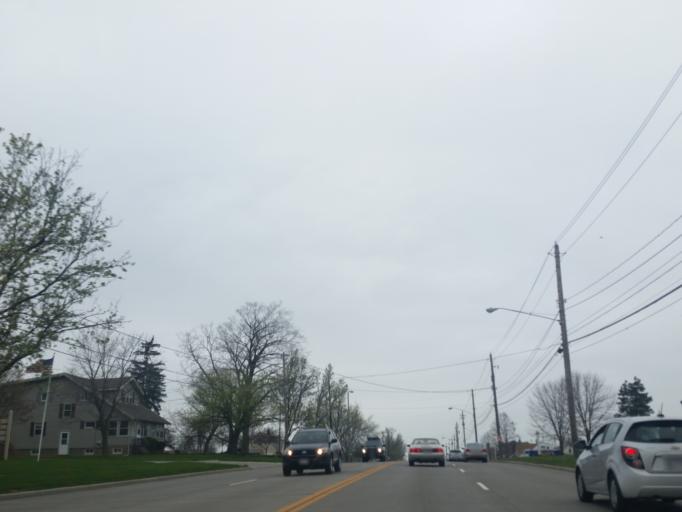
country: US
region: Ohio
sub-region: Cuyahoga County
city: Brooklyn
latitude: 41.4353
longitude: -81.7352
